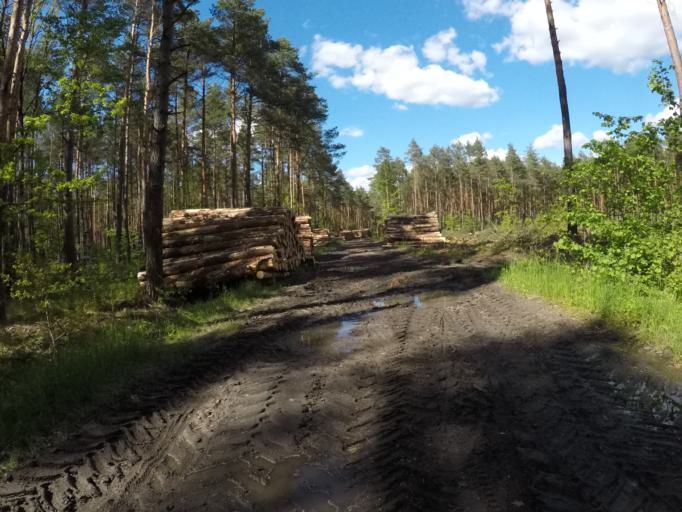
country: PL
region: Swietokrzyskie
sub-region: Powiat kielecki
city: Kostomloty Drugie
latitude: 50.8891
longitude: 20.5381
